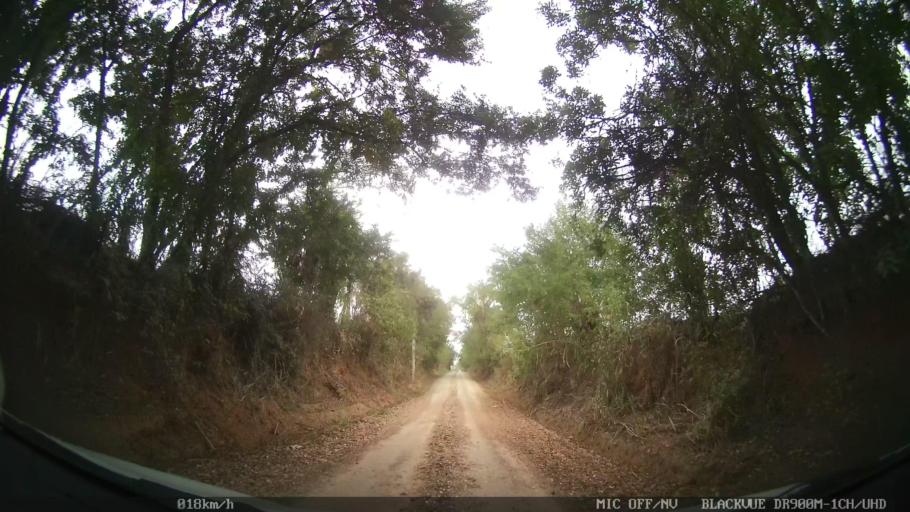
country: BR
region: Sao Paulo
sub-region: Americana
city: Americana
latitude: -22.6587
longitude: -47.3694
